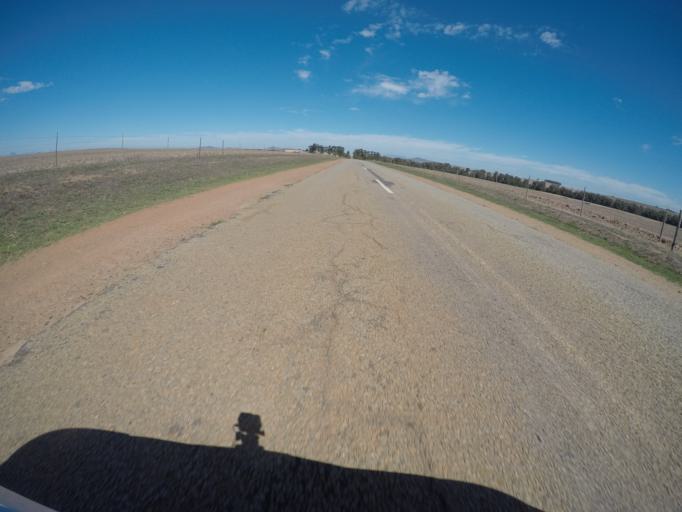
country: ZA
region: Western Cape
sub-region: City of Cape Town
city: Atlantis
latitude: -33.6064
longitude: 18.6391
